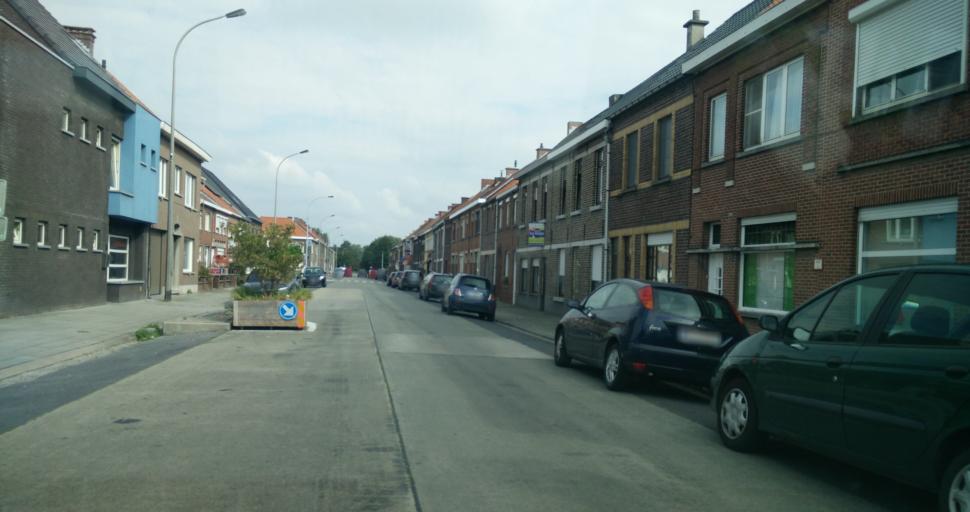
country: BE
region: Flanders
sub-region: Provincie Oost-Vlaanderen
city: Oudenaarde
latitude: 50.8511
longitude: 3.6138
